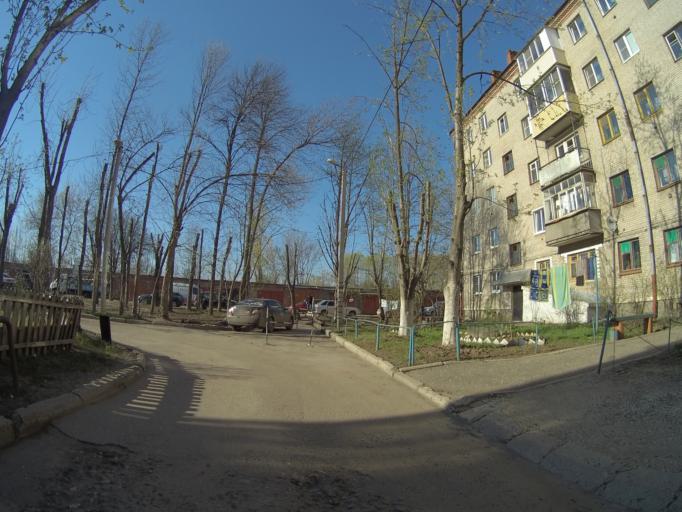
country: RU
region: Vladimir
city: Vladimir
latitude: 56.1505
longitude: 40.4201
